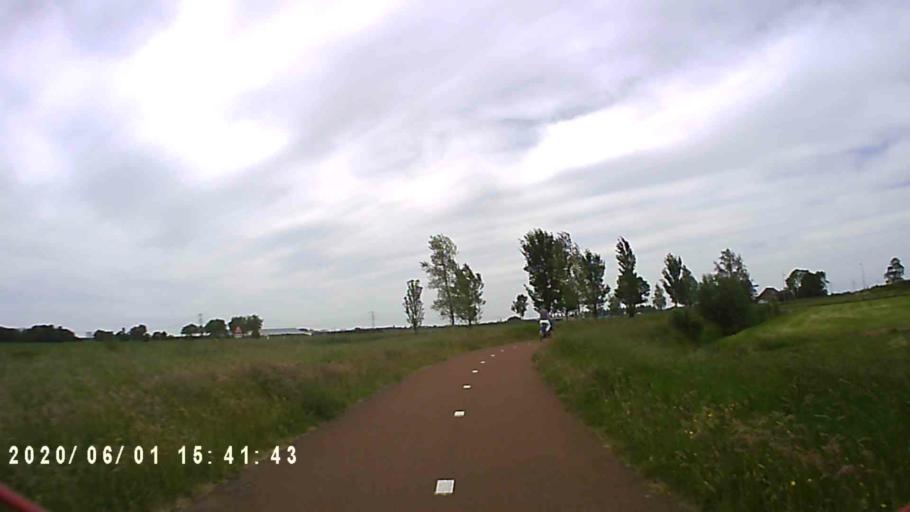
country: NL
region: Friesland
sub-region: Gemeente Boarnsterhim
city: Wergea
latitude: 53.1571
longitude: 5.8253
